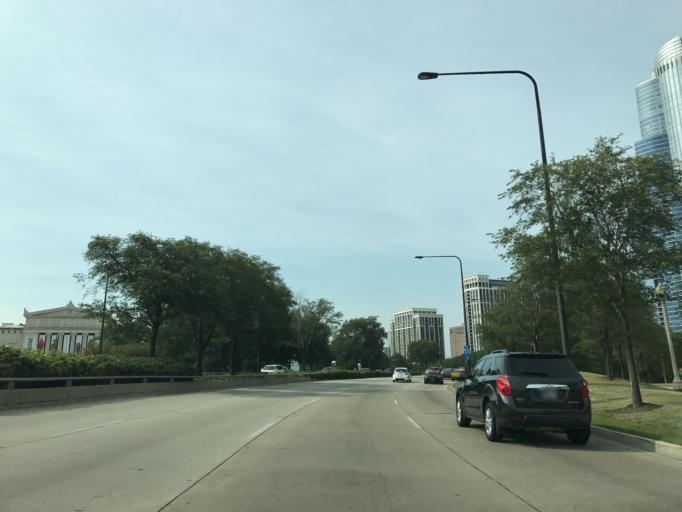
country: US
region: Illinois
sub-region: Cook County
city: Chicago
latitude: 41.8696
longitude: -87.6173
